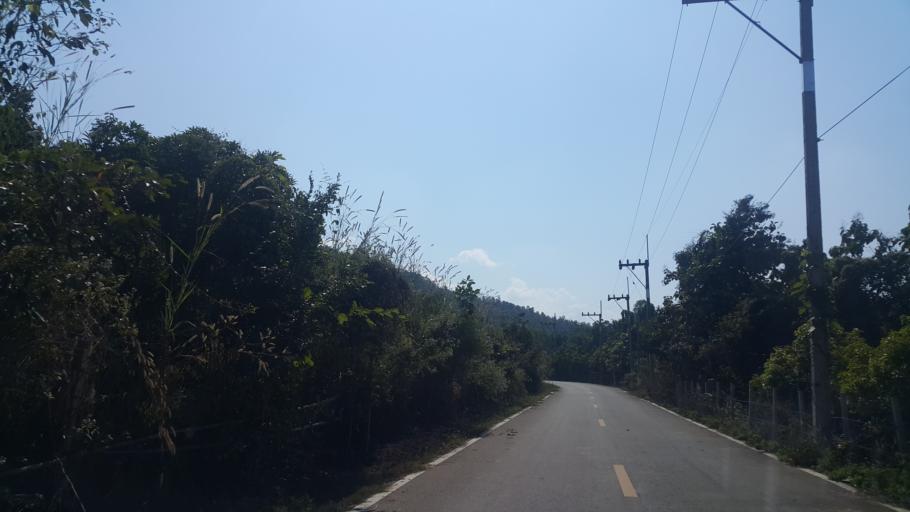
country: TH
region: Chiang Mai
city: San Kamphaeng
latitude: 18.6914
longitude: 99.1693
